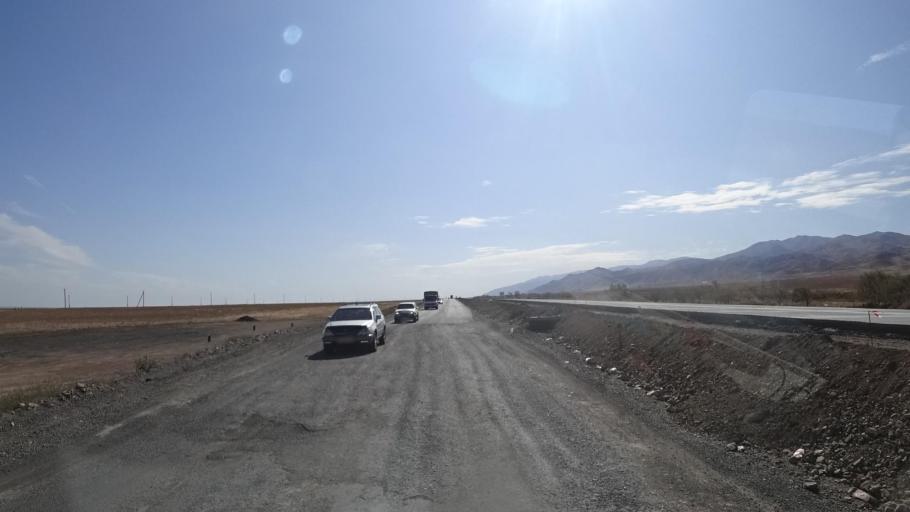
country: KG
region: Chuy
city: Ivanovka
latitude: 43.3992
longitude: 75.1176
